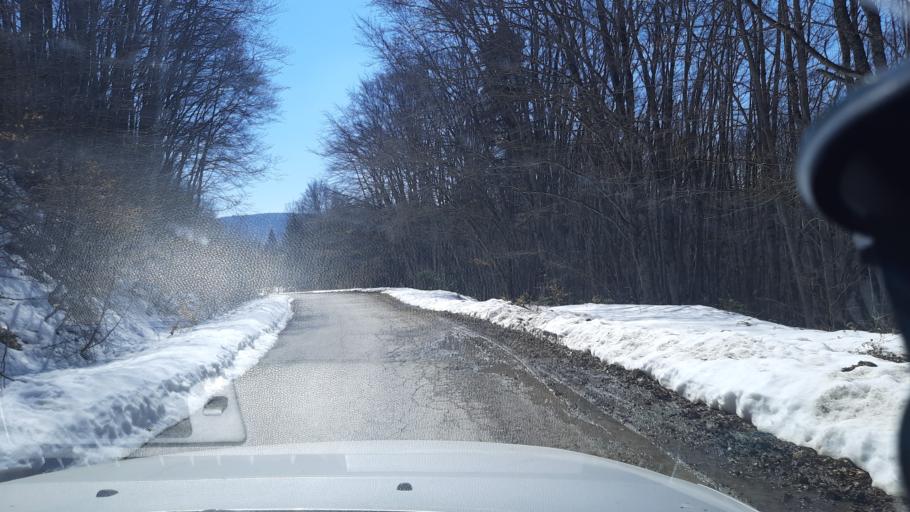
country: MK
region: Gostivar
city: Vrutok
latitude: 41.7084
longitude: 20.7386
